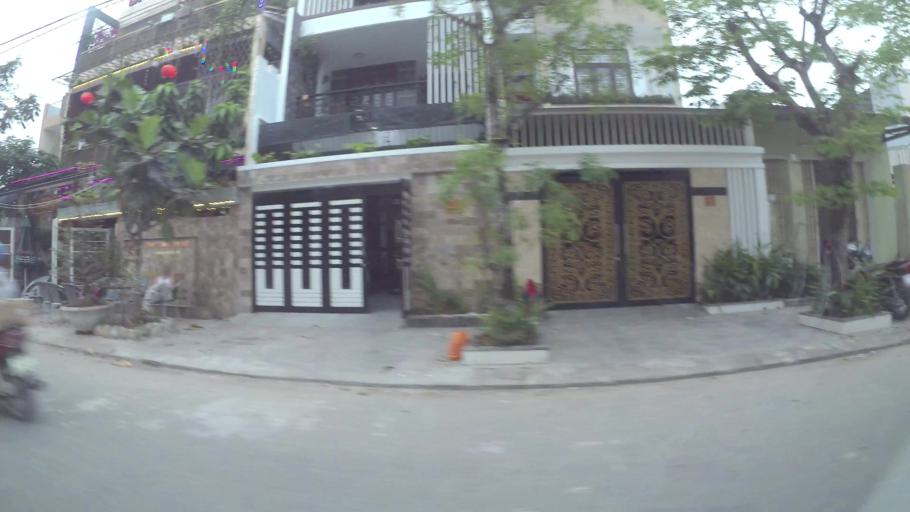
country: VN
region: Da Nang
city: Thanh Khe
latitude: 16.0474
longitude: 108.1800
